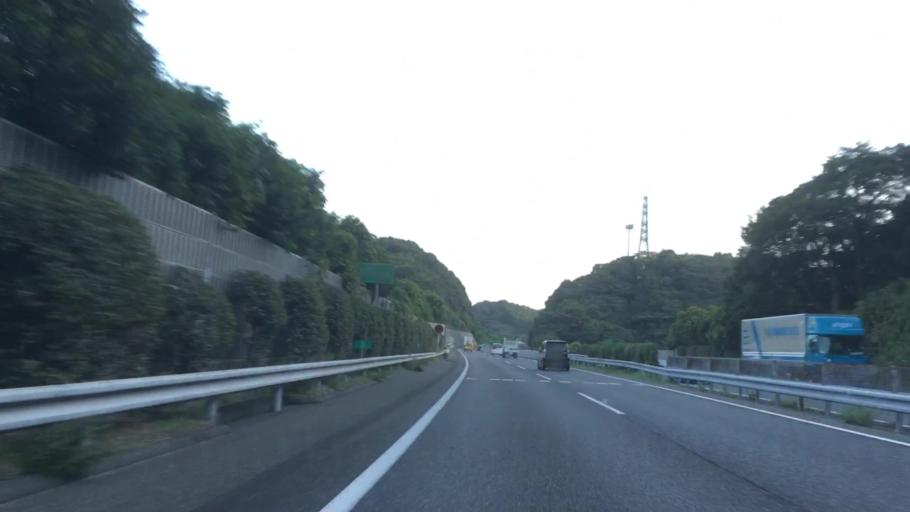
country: JP
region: Yamaguchi
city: Shimonoseki
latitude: 33.9002
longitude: 130.9716
